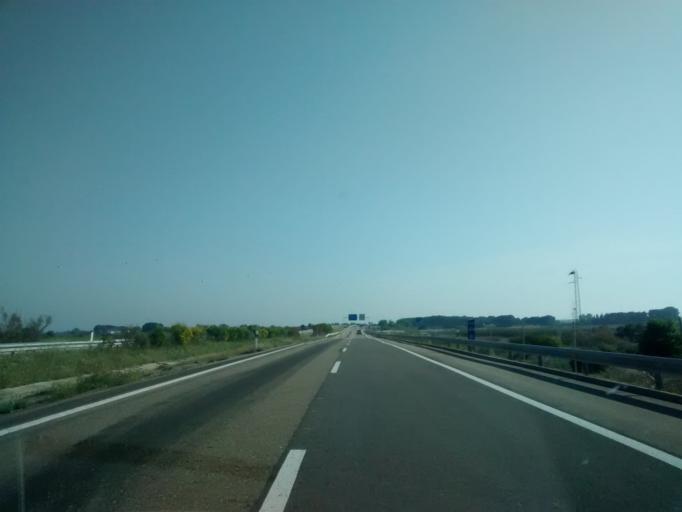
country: ES
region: Aragon
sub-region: Provincia de Zaragoza
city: Zuera
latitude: 41.9041
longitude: -0.7614
